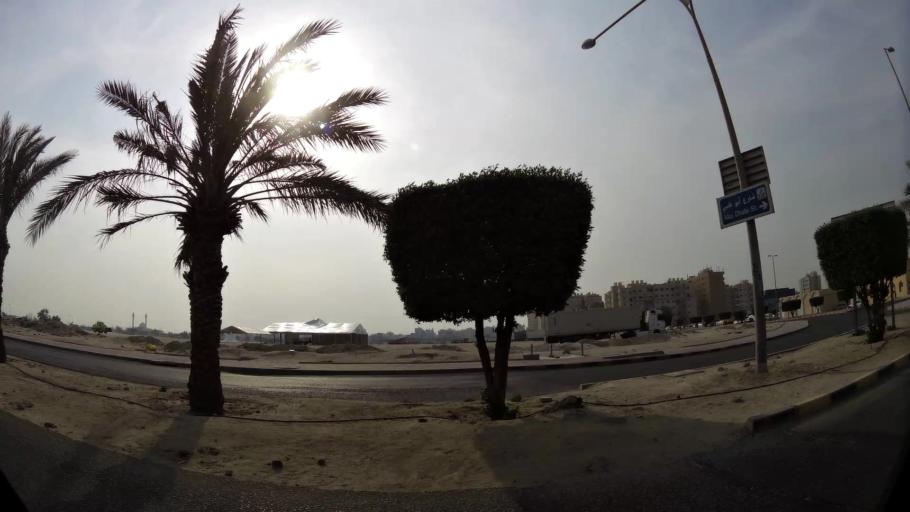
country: KW
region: Al Farwaniyah
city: Janub as Surrah
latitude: 29.2765
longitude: 47.9781
